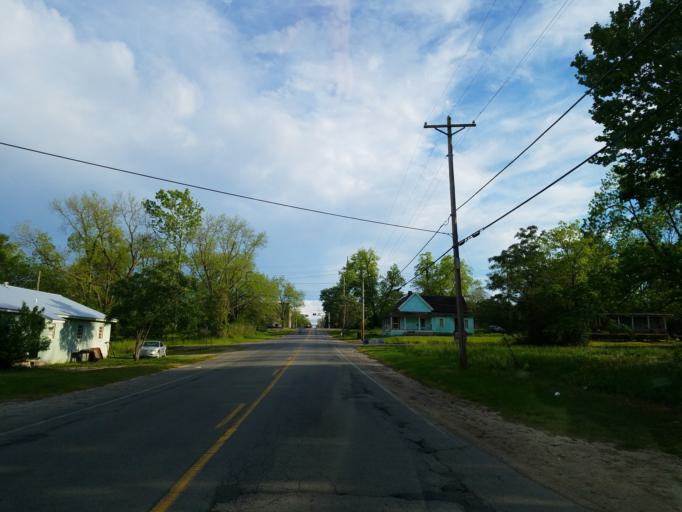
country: US
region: Georgia
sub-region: Crisp County
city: Cordele
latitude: 31.9724
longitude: -83.7882
